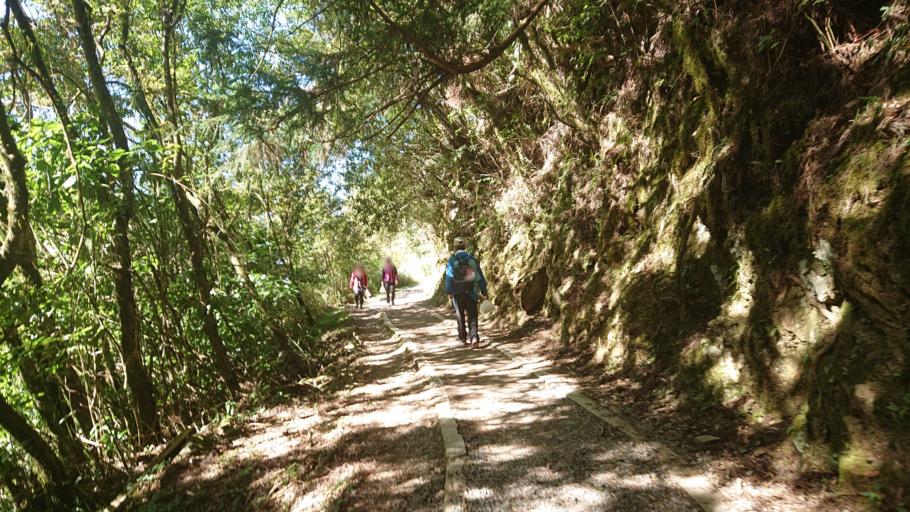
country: TW
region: Taiwan
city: Lugu
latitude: 23.4795
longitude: 120.8256
